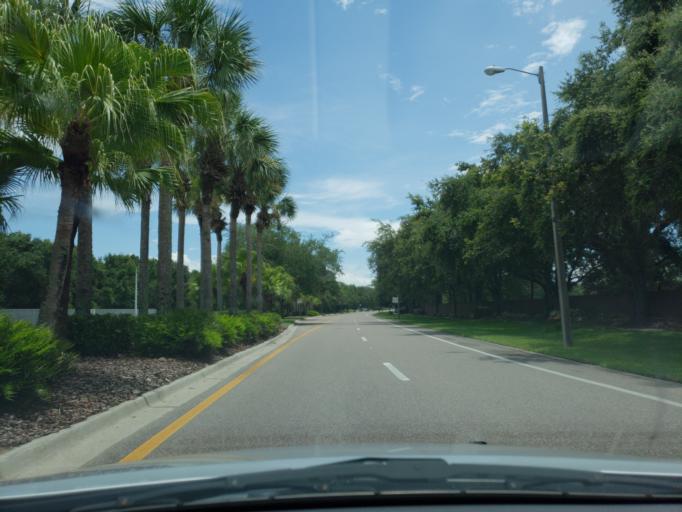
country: US
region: Florida
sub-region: Hillsborough County
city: Pebble Creek
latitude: 28.1207
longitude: -82.3827
